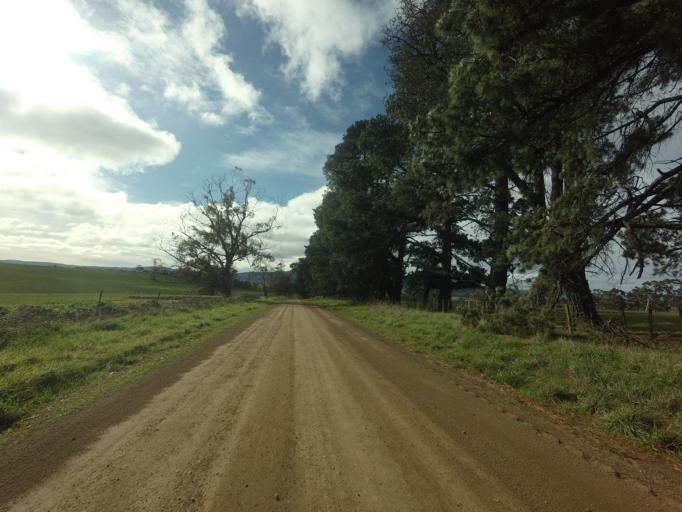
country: AU
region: Tasmania
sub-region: Derwent Valley
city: New Norfolk
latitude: -42.7165
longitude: 146.8807
